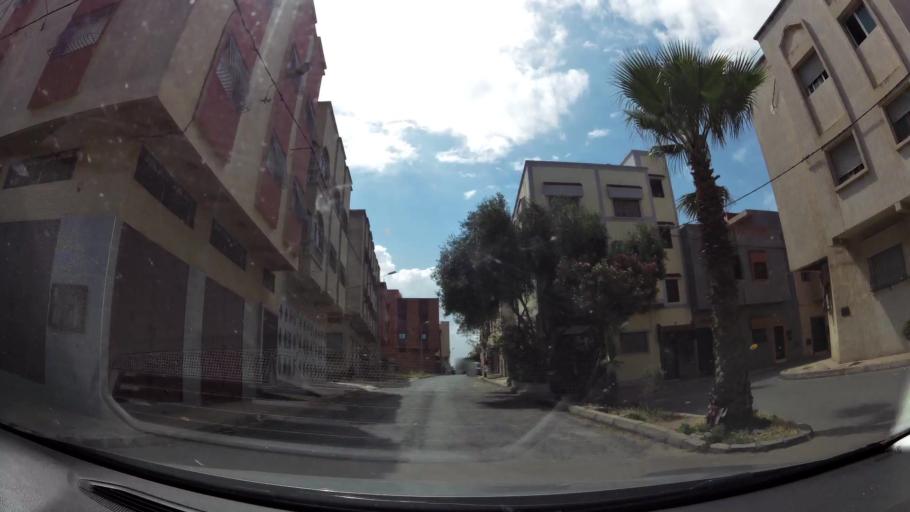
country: MA
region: Rabat-Sale-Zemmour-Zaer
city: Sale
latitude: 34.0715
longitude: -6.7929
